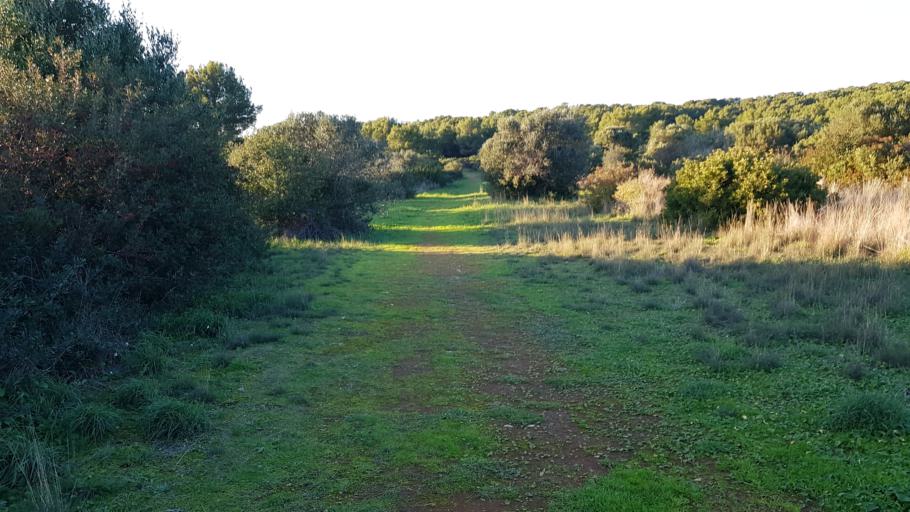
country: IT
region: Apulia
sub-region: Provincia di Lecce
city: Nardo
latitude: 40.1518
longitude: 17.9652
